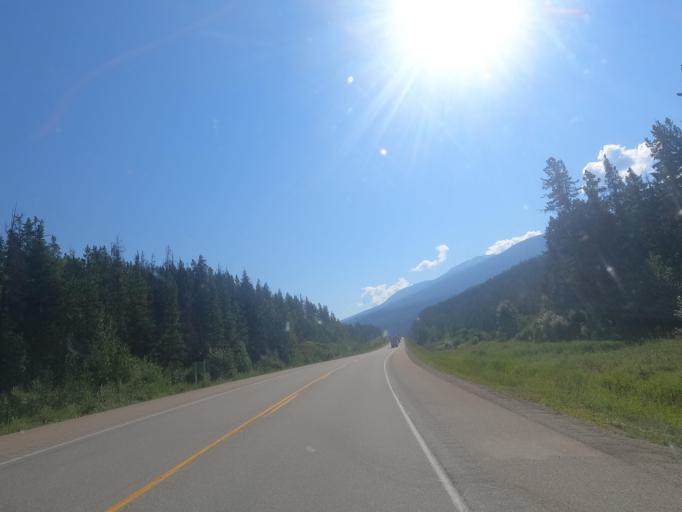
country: CA
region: Alberta
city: Jasper Park Lodge
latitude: 52.8877
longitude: -118.4727
